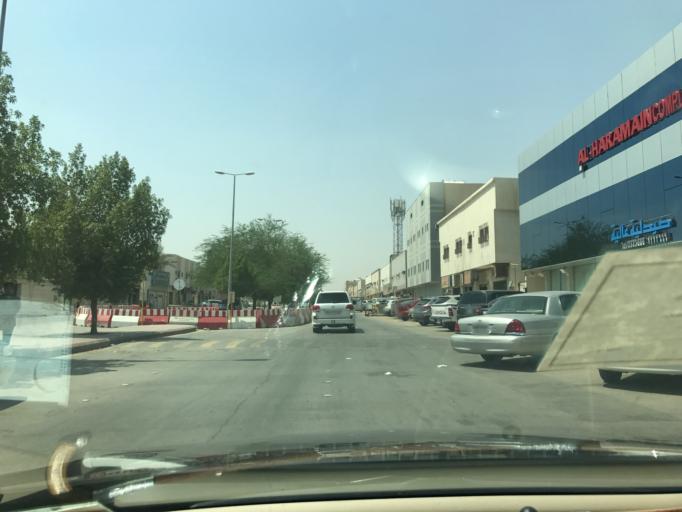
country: SA
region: Ar Riyad
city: Riyadh
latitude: 24.7476
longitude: 46.7727
